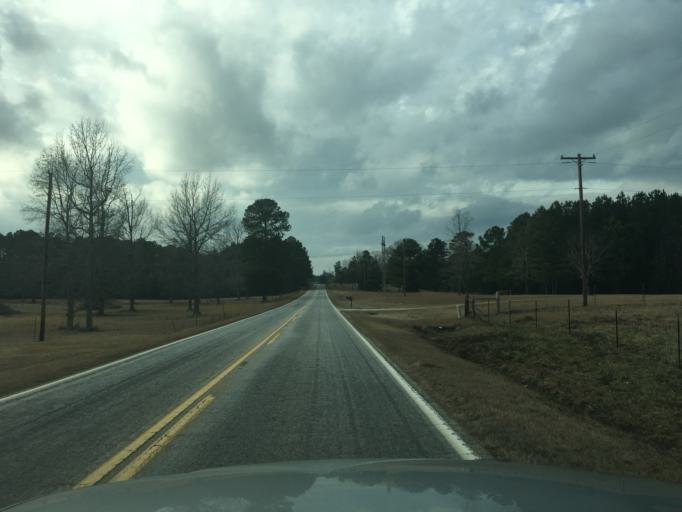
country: US
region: South Carolina
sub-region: Abbeville County
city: Abbeville
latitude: 34.2404
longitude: -82.4018
